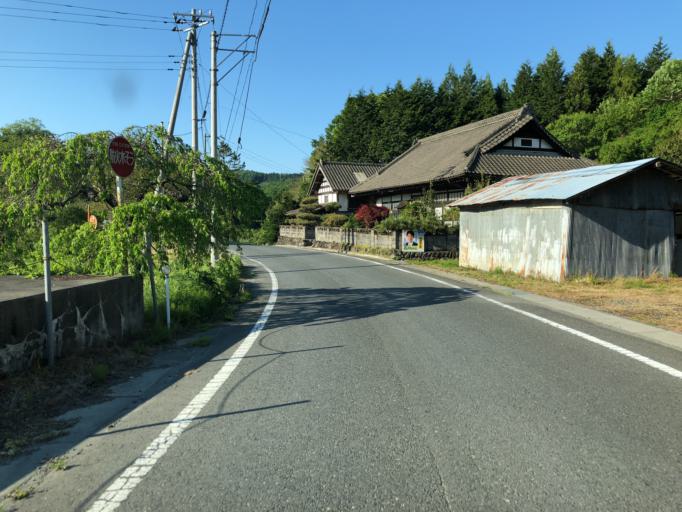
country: JP
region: Ibaraki
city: Kitaibaraki
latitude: 36.9148
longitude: 140.5809
